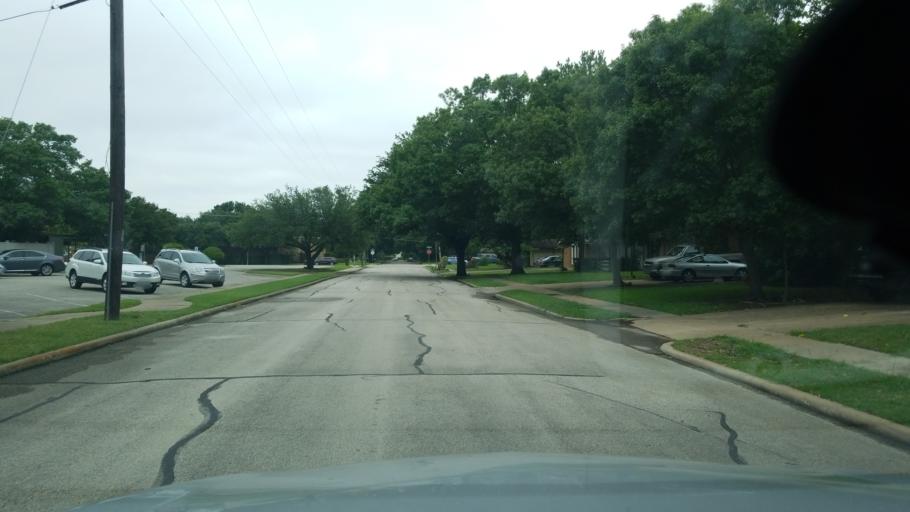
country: US
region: Texas
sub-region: Dallas County
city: Irving
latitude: 32.8529
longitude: -96.9490
